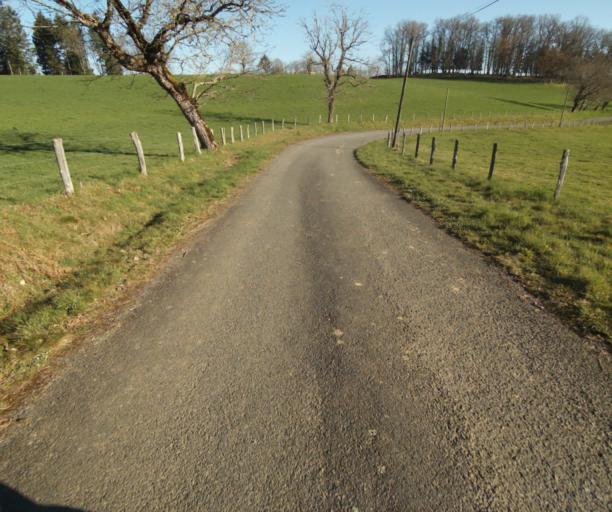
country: FR
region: Limousin
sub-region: Departement de la Correze
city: Seilhac
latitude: 45.3546
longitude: 1.7460
